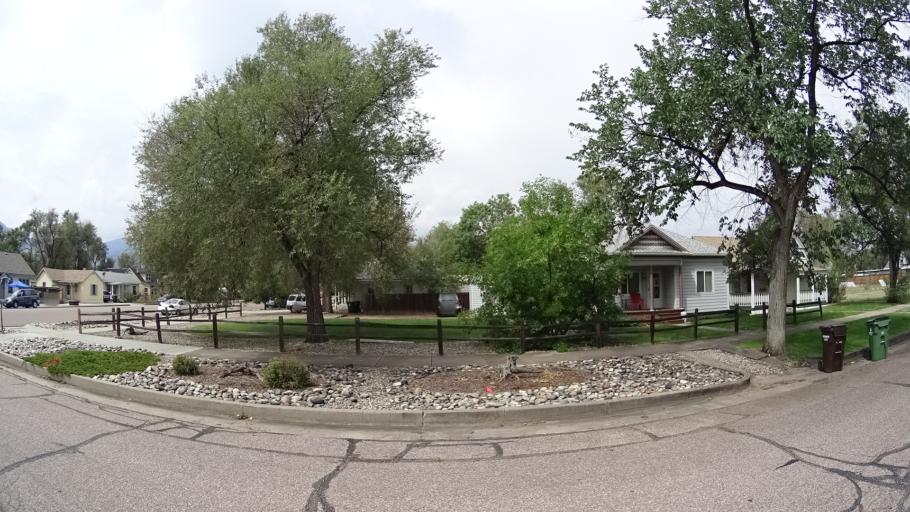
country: US
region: Colorado
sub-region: El Paso County
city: Colorado Springs
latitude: 38.8221
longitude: -104.8260
